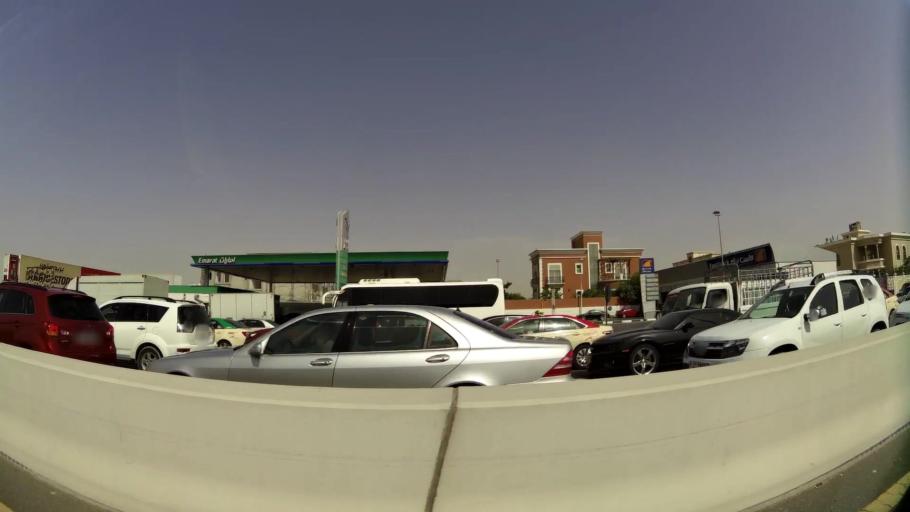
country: AE
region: Ash Shariqah
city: Sharjah
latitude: 25.2646
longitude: 55.3922
